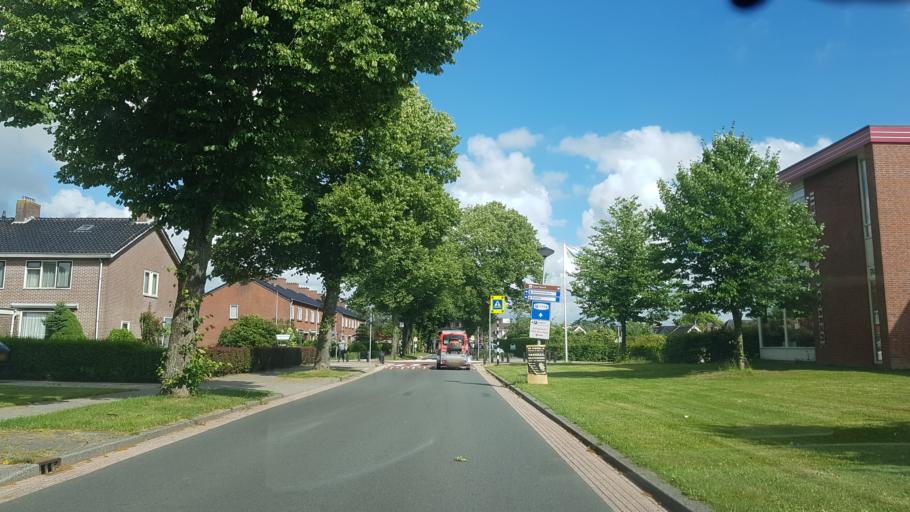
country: NL
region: Groningen
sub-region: Gemeente Bedum
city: Bedum
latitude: 53.4049
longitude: 6.6710
